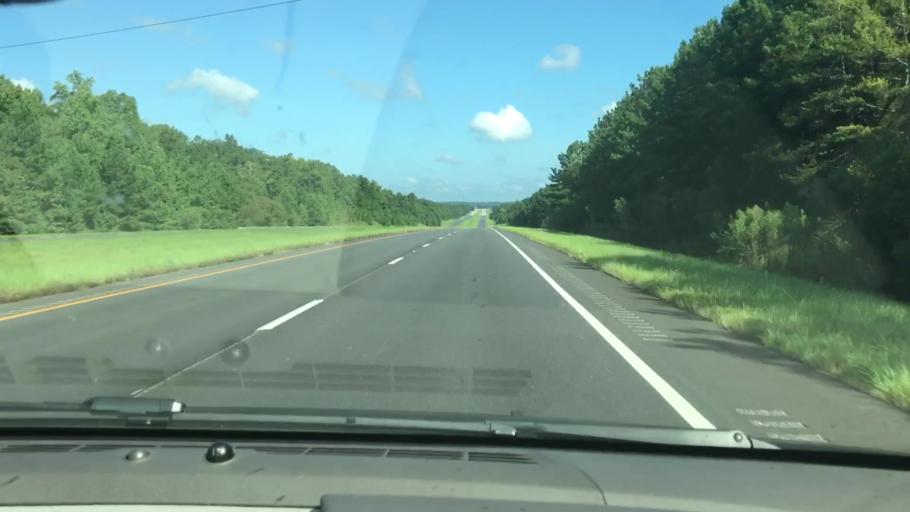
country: US
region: Alabama
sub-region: Barbour County
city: Eufaula
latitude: 32.0475
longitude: -85.1316
